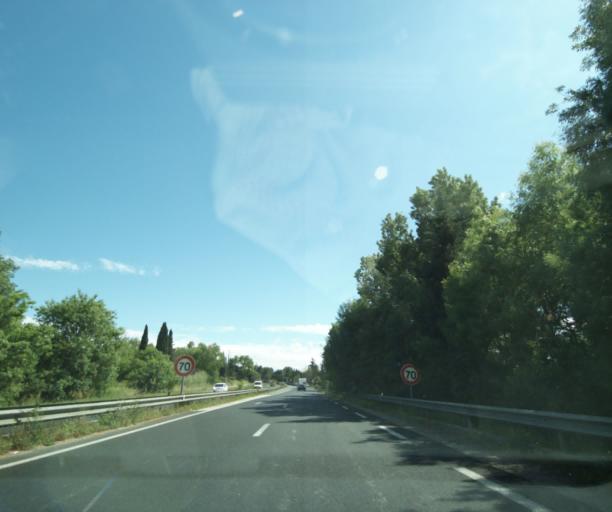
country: FR
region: Languedoc-Roussillon
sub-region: Departement de l'Herault
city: Laverune
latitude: 43.5962
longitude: 3.8200
